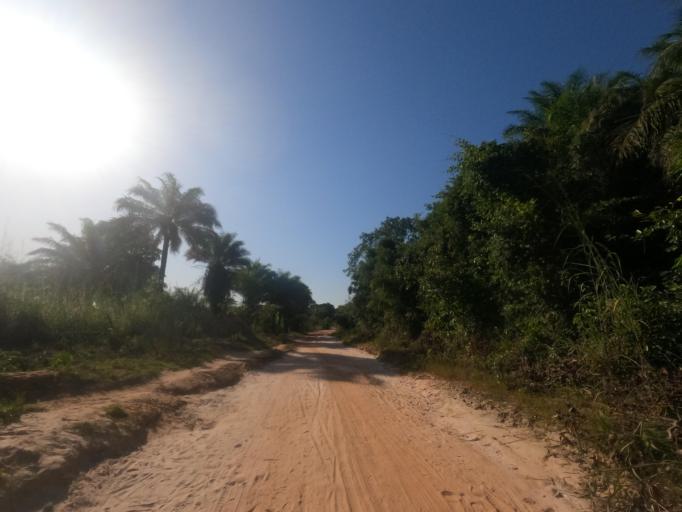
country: GW
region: Cacheu
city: Cacheu
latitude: 12.3929
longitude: -16.2234
